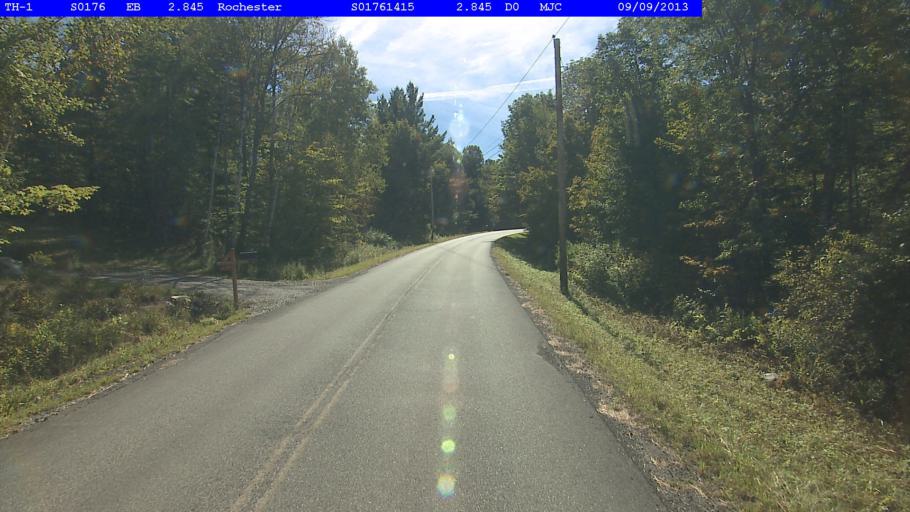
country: US
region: Vermont
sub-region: Orange County
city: Randolph
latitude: 43.8634
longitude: -72.7630
